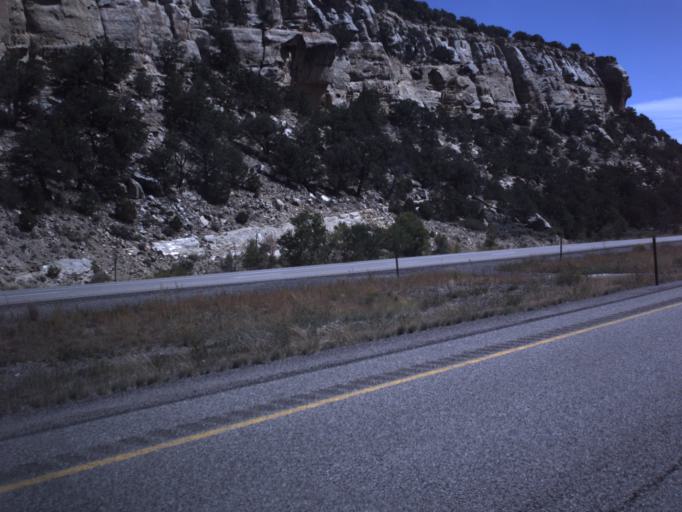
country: US
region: Utah
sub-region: Wayne County
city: Loa
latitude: 38.7585
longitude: -111.4492
